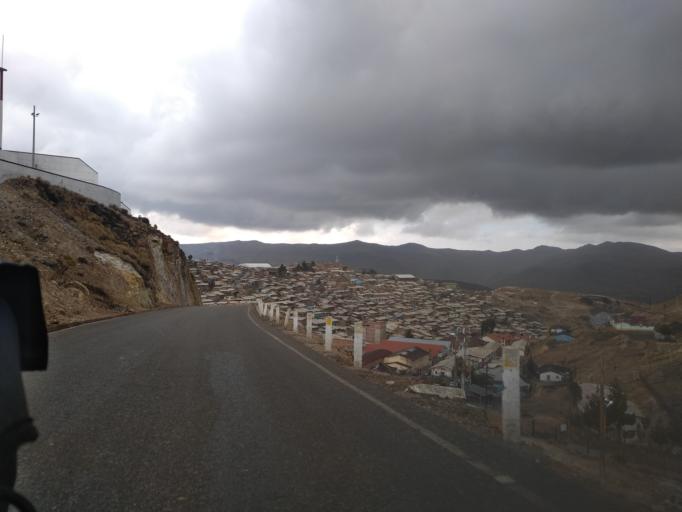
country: PE
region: La Libertad
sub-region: Provincia de Santiago de Chuco
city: Quiruvilca
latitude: -7.9993
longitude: -78.3088
